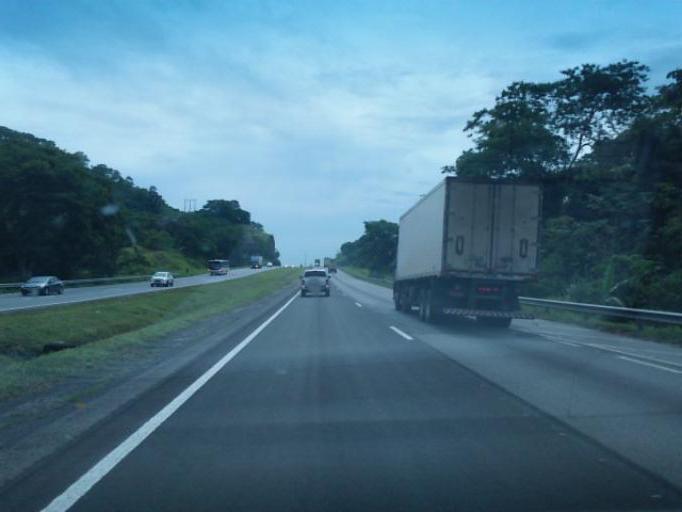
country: BR
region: Sao Paulo
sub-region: Juquia
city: Juquia
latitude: -24.3227
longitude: -47.5445
